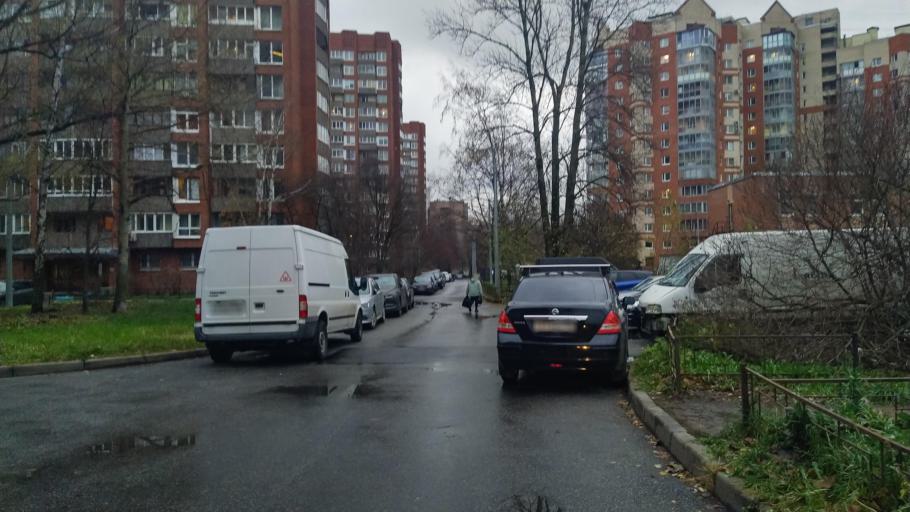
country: RU
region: St.-Petersburg
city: Grazhdanka
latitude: 60.0318
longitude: 30.4245
